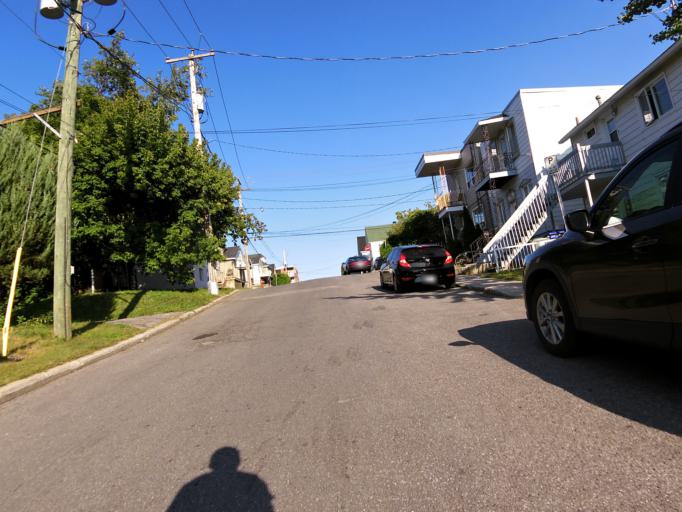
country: CA
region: Ontario
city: Ottawa
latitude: 45.4317
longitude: -75.7243
